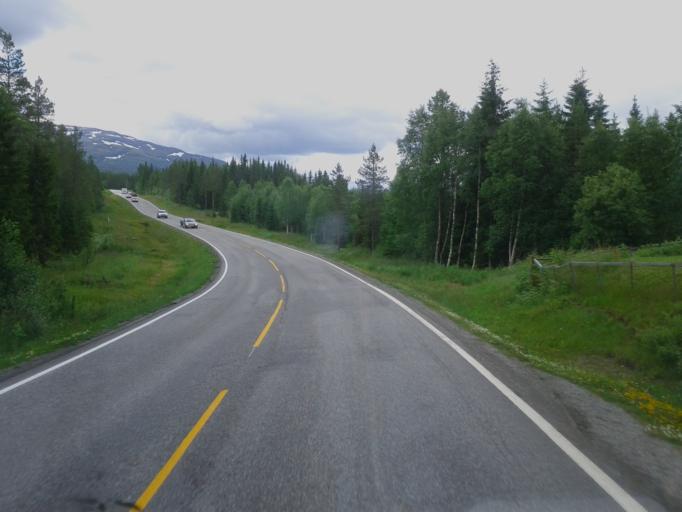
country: NO
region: Nord-Trondelag
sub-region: Hoylandet
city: Hoylandet
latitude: 64.6597
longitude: 12.6488
